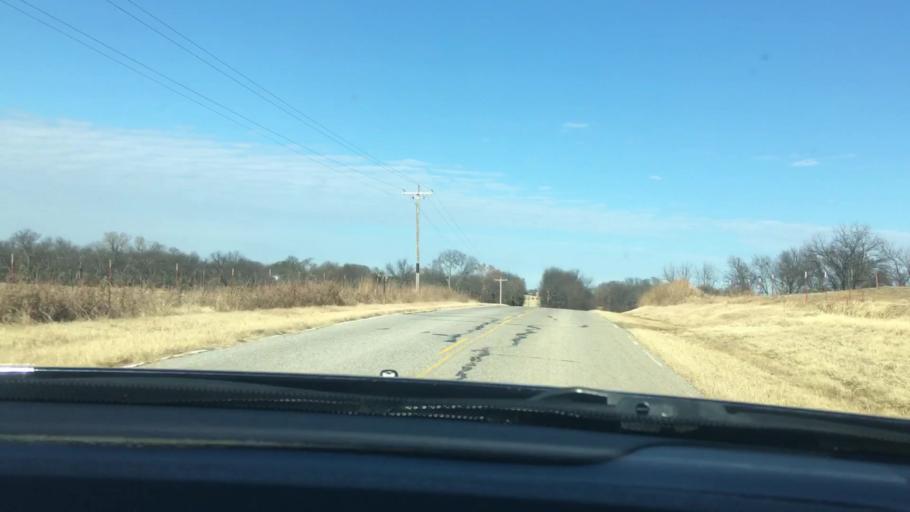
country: US
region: Oklahoma
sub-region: Garvin County
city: Wynnewood
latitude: 34.7190
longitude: -97.1254
